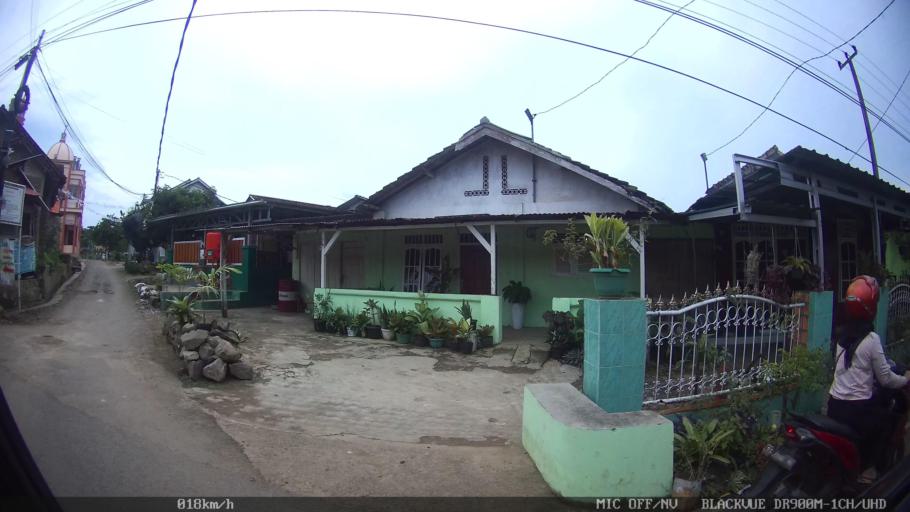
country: ID
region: Lampung
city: Kedaton
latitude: -5.3900
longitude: 105.1975
